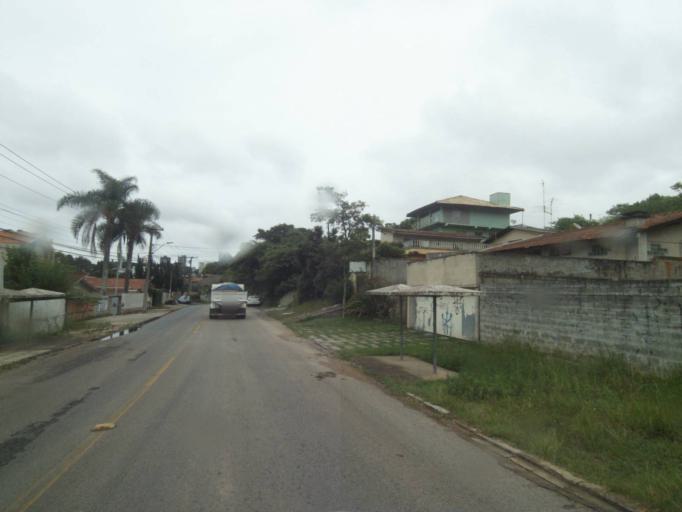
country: BR
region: Parana
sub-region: Curitiba
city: Curitiba
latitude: -25.4265
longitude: -49.3252
